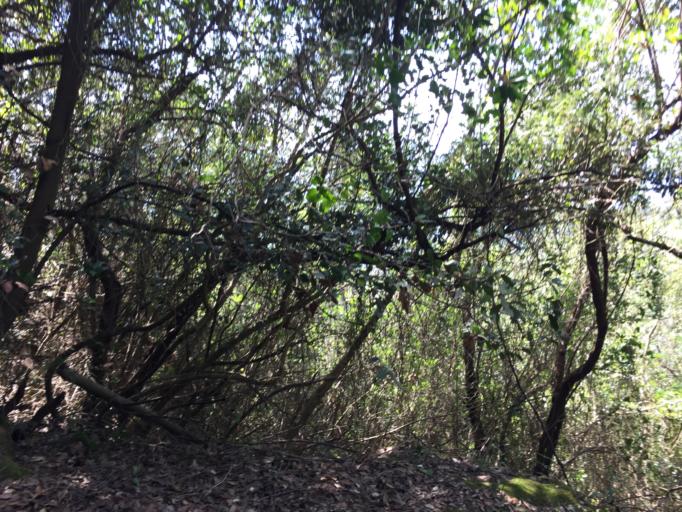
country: IT
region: Liguria
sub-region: Provincia di Genova
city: Santa Margherita Ligure
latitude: 44.3223
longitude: 9.1787
